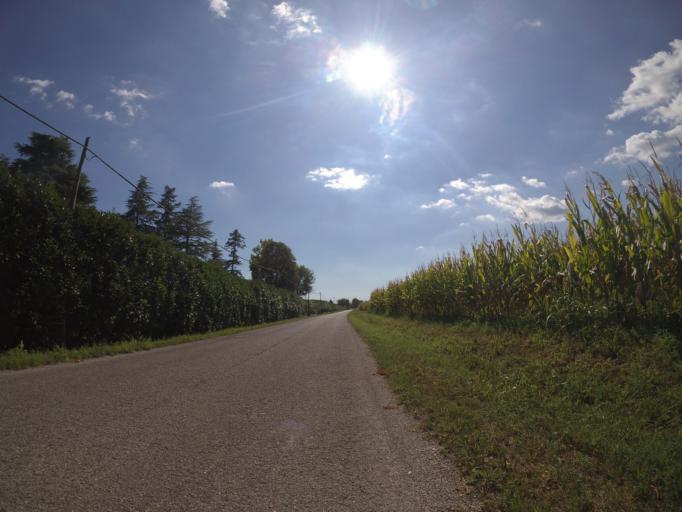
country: IT
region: Friuli Venezia Giulia
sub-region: Provincia di Udine
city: Talmassons
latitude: 45.9280
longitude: 13.1432
